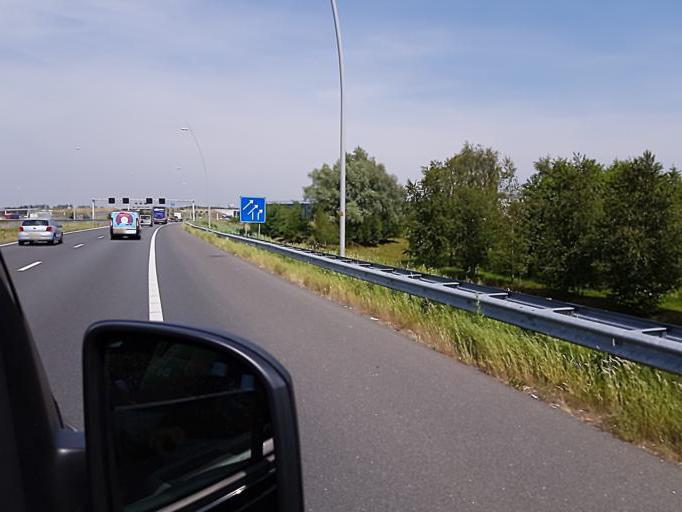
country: NL
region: North Brabant
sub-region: Gemeente Eindhoven
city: Meerhoven
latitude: 51.4756
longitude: 5.4049
